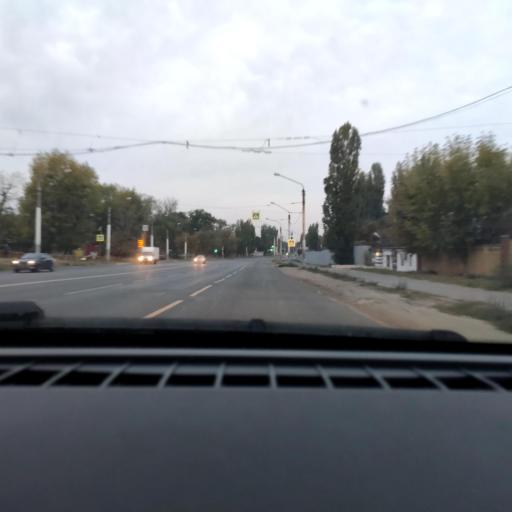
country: RU
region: Voronezj
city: Maslovka
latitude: 51.5997
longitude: 39.2476
